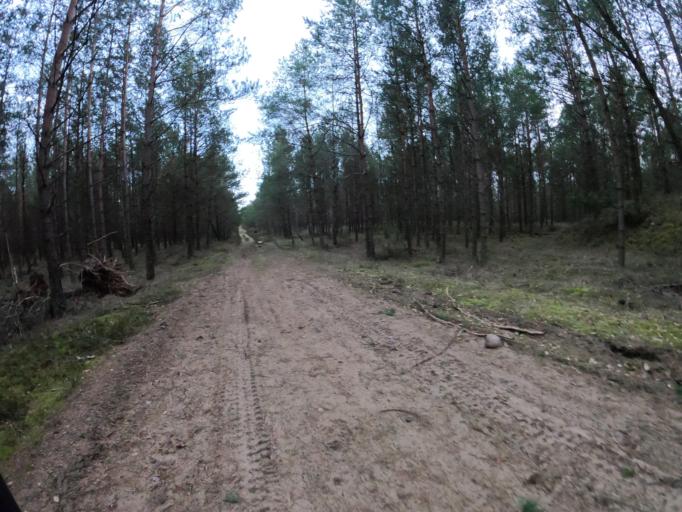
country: PL
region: West Pomeranian Voivodeship
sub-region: Powiat szczecinecki
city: Borne Sulinowo
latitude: 53.5598
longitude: 16.5638
